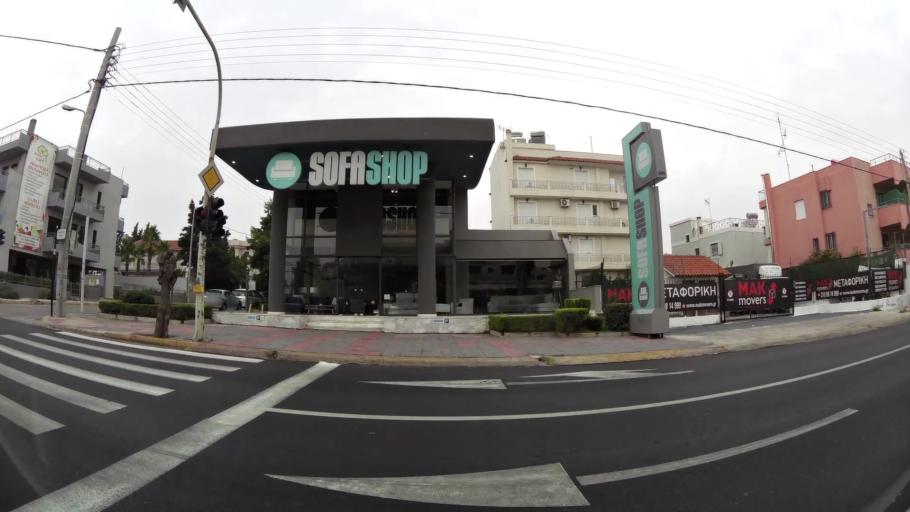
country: GR
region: Attica
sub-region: Nomarchia Athinas
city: Alimos
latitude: 37.9073
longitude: 23.7330
